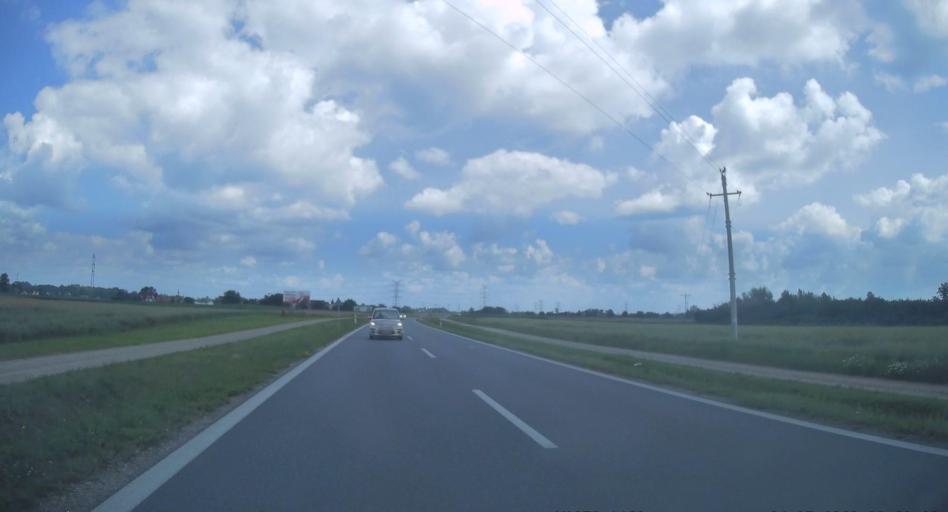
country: PL
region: Lesser Poland Voivodeship
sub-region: Powiat tarnowski
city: Wojnicz
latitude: 49.9382
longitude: 20.8444
